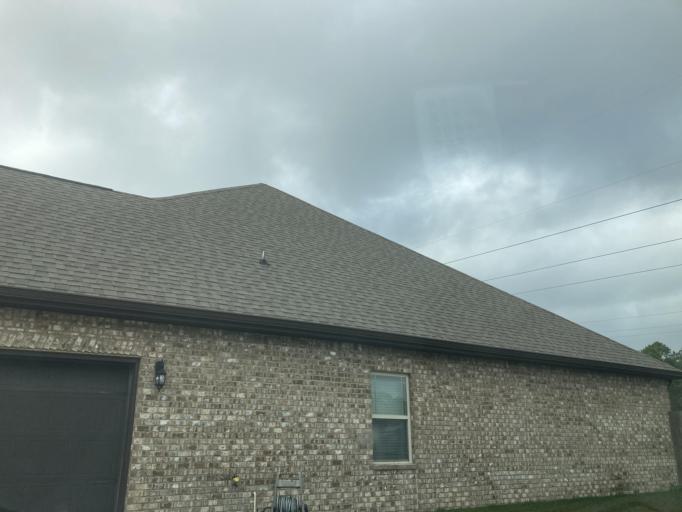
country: US
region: Mississippi
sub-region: Harrison County
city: D'Iberville
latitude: 30.4788
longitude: -88.9828
